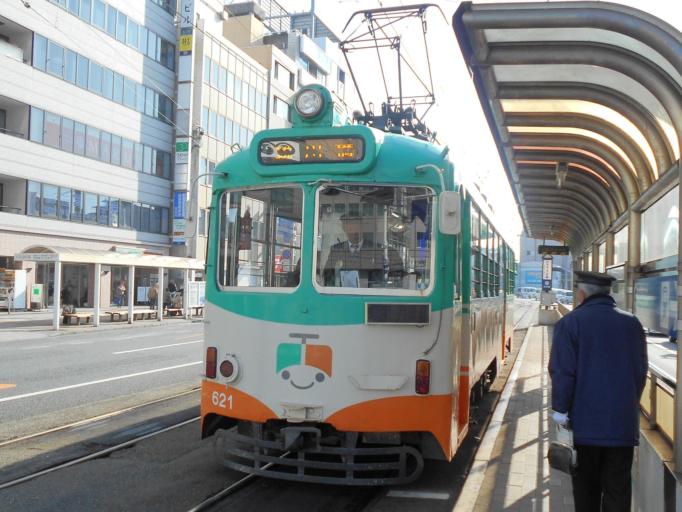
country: JP
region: Kochi
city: Kochi-shi
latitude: 33.5595
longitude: 133.5433
